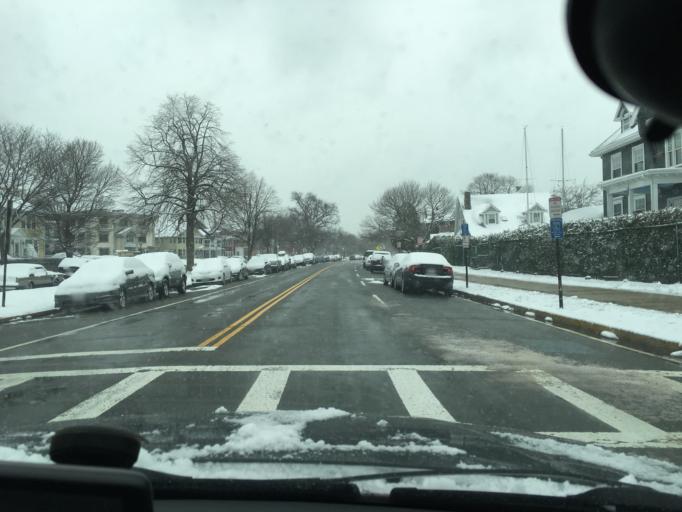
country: US
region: Massachusetts
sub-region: Suffolk County
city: South Boston
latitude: 42.3317
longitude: -71.0290
